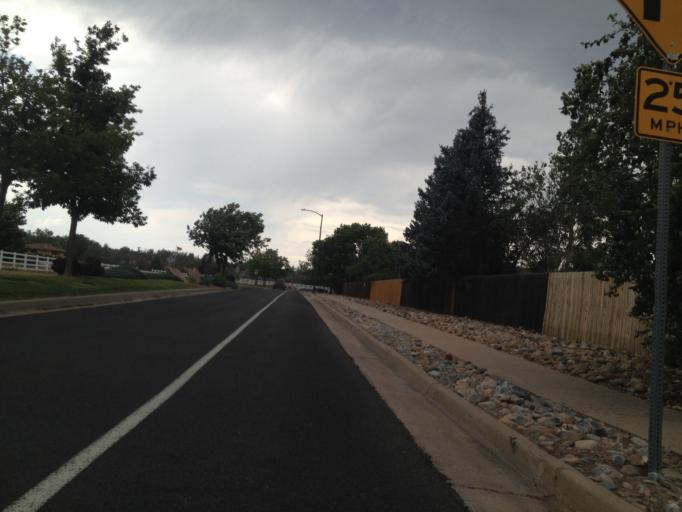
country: US
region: Colorado
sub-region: Boulder County
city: Louisville
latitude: 39.9666
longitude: -105.1421
